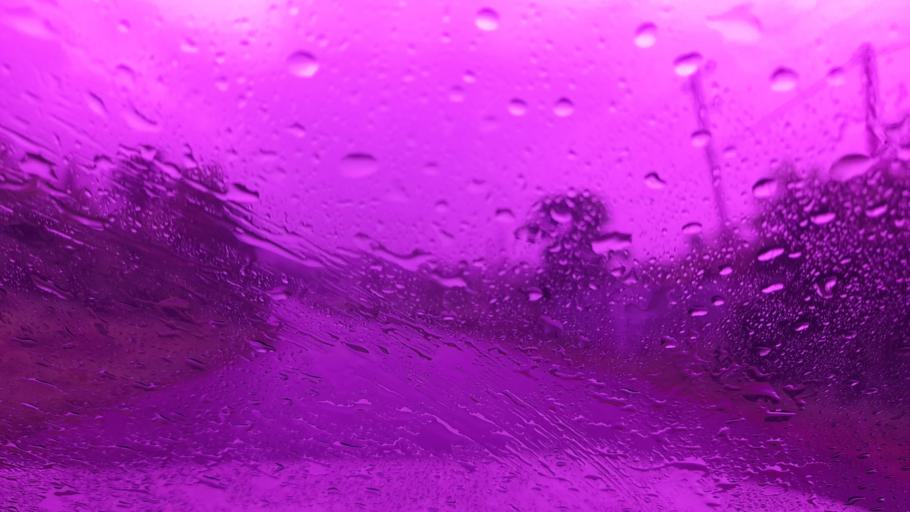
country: ET
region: Oromiya
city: Jima
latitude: 7.7198
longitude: 37.1061
